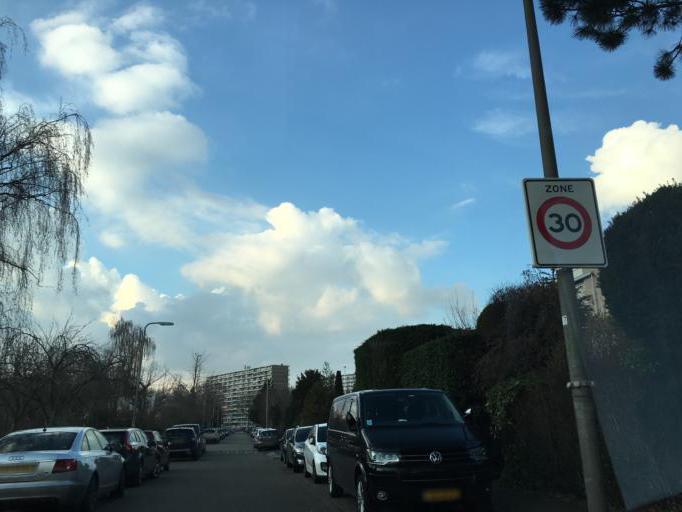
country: NL
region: South Holland
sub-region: Gemeente Capelle aan den IJssel
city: Capelle aan den IJssel
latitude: 51.9237
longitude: 4.5774
